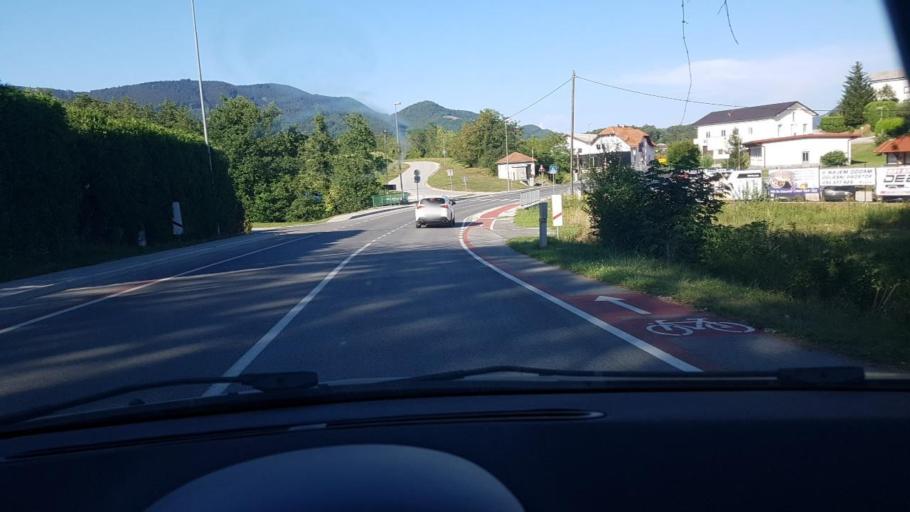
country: SI
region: Rogaska Slatina
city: Rogaska Slatina
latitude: 46.2397
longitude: 15.6172
